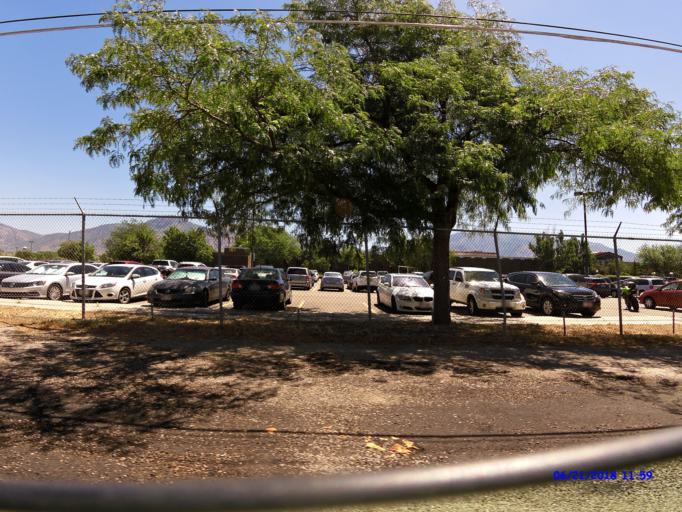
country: US
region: Utah
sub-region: Weber County
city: Marriott-Slaterville
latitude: 41.2474
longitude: -112.0095
